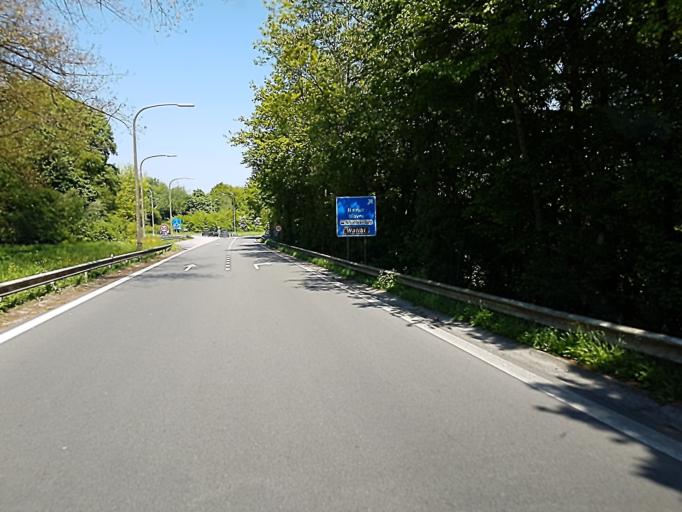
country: BE
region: Wallonia
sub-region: Province du Brabant Wallon
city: Nivelles
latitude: 50.5855
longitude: 4.3065
